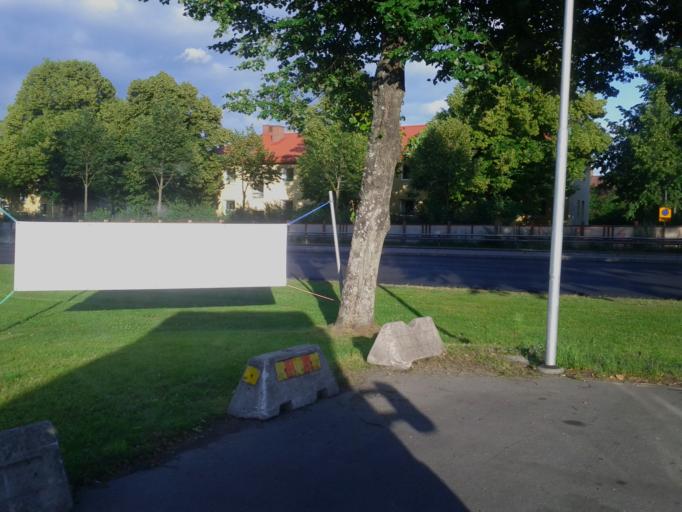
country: SE
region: Dalarna
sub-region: Borlange Kommun
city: Borlaenge
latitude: 60.4788
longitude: 15.4387
